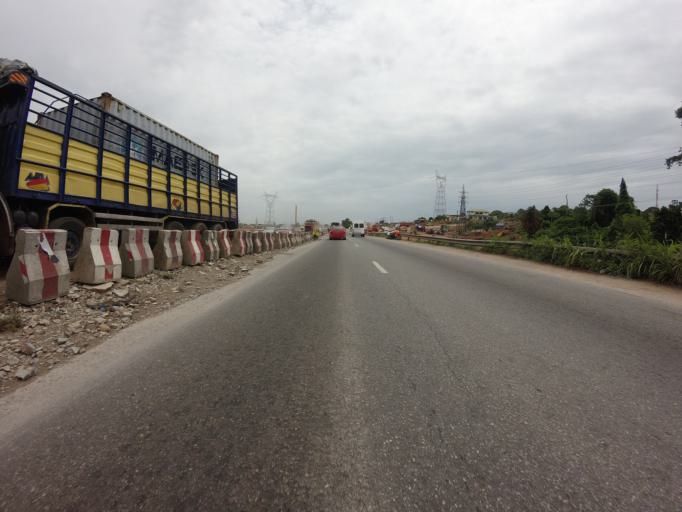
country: GH
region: Greater Accra
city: Dome
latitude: 5.6827
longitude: -0.2756
